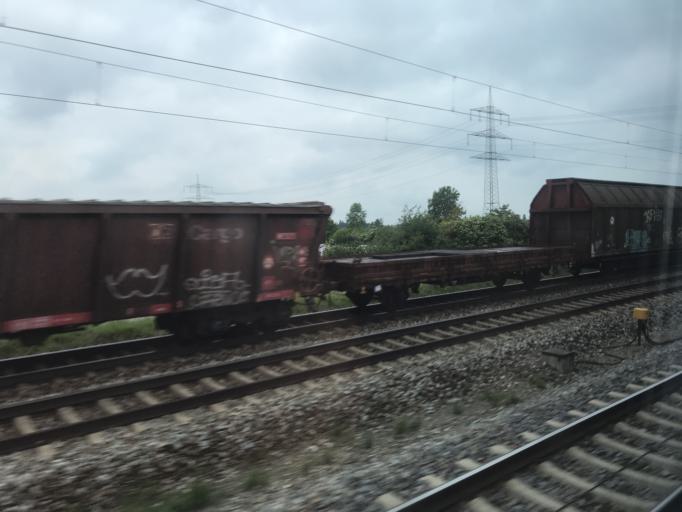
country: DE
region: Bavaria
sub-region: Swabia
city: Mering
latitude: 48.2803
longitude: 10.9663
